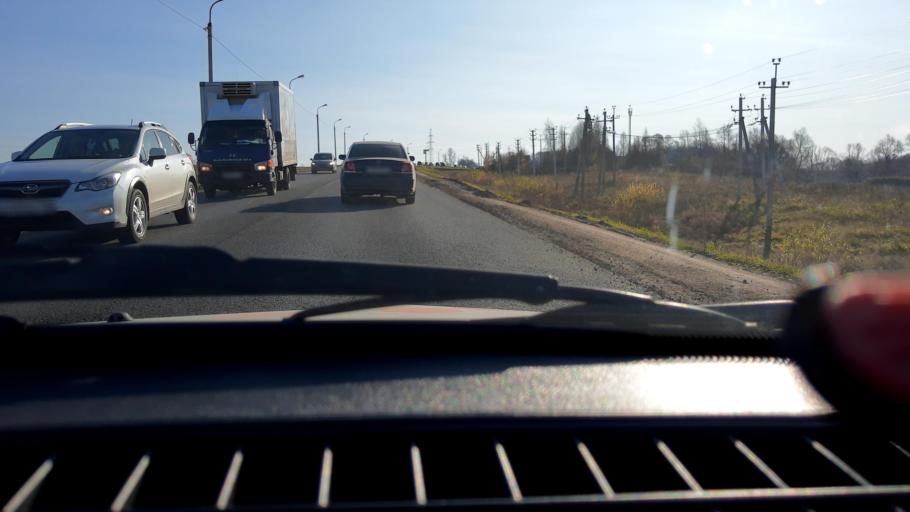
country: RU
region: Bashkortostan
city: Kabakovo
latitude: 54.6383
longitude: 56.0914
